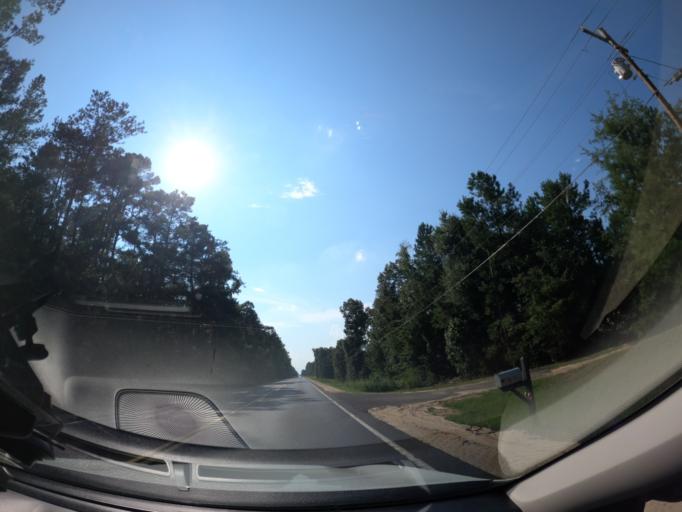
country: US
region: South Carolina
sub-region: Aiken County
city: New Ellenton
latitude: 33.3998
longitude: -81.7588
